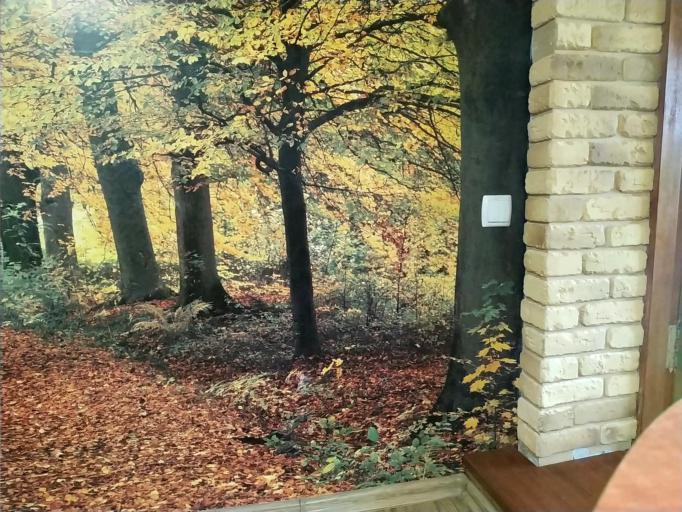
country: RU
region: Smolensk
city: Dorogobuzh
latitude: 54.8398
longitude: 33.3297
